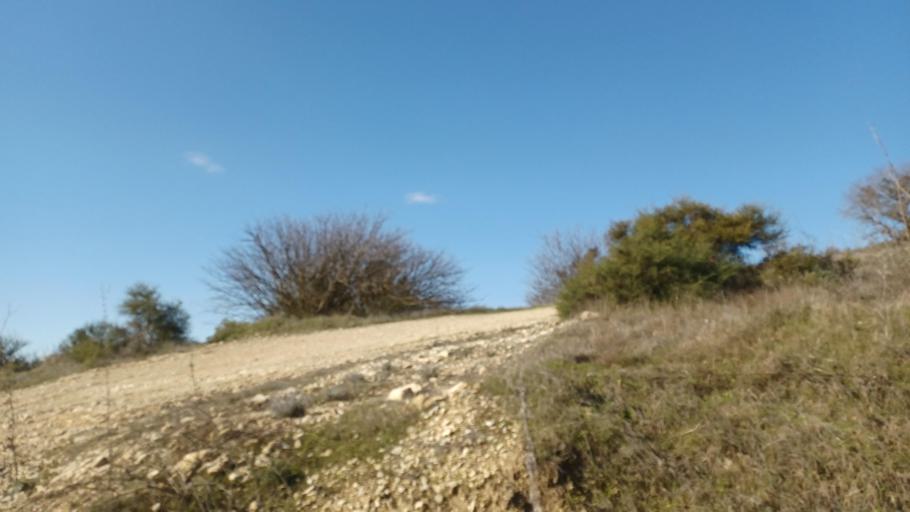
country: CY
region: Limassol
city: Pachna
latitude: 34.8123
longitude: 32.6692
